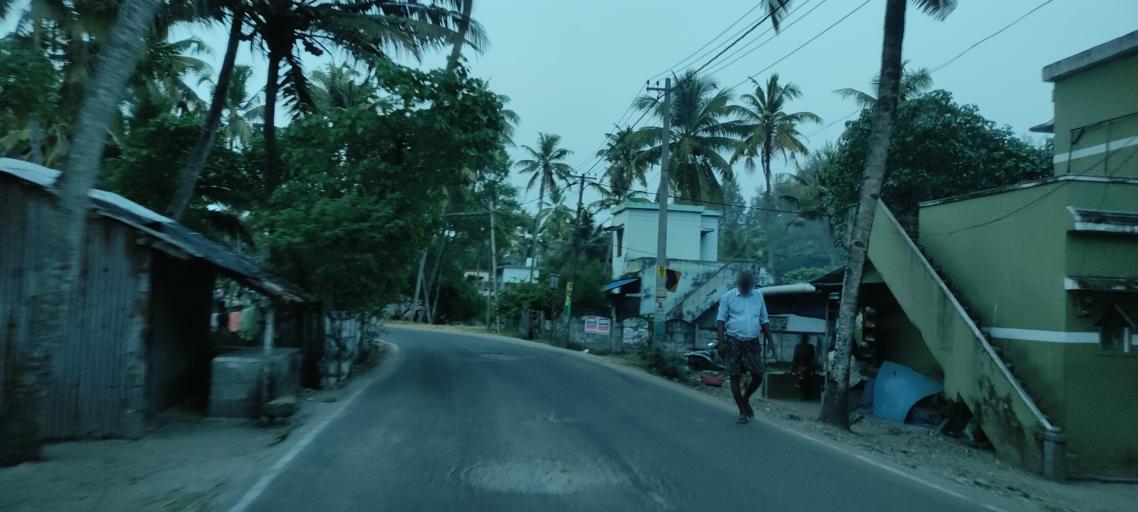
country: IN
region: Kerala
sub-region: Alappuzha
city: Kayankulam
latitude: 9.1297
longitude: 76.4661
